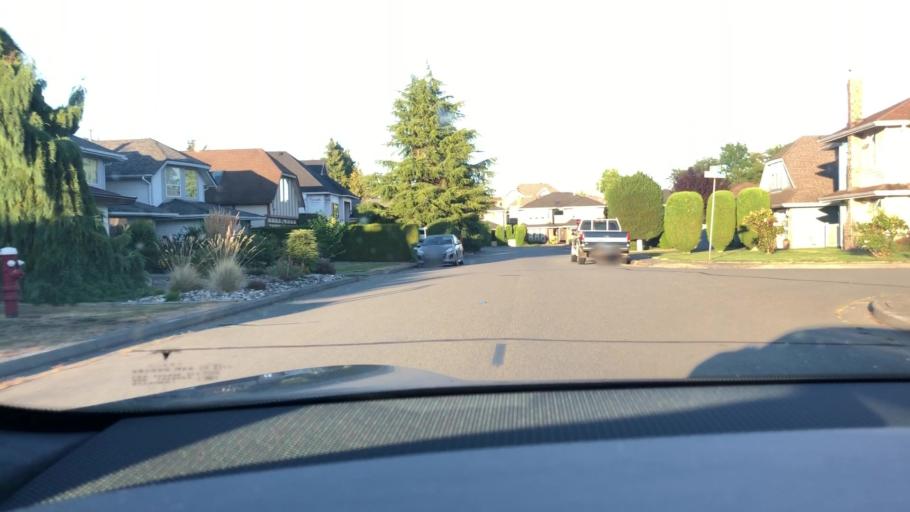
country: CA
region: British Columbia
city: Richmond
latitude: 49.1459
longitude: -123.1617
